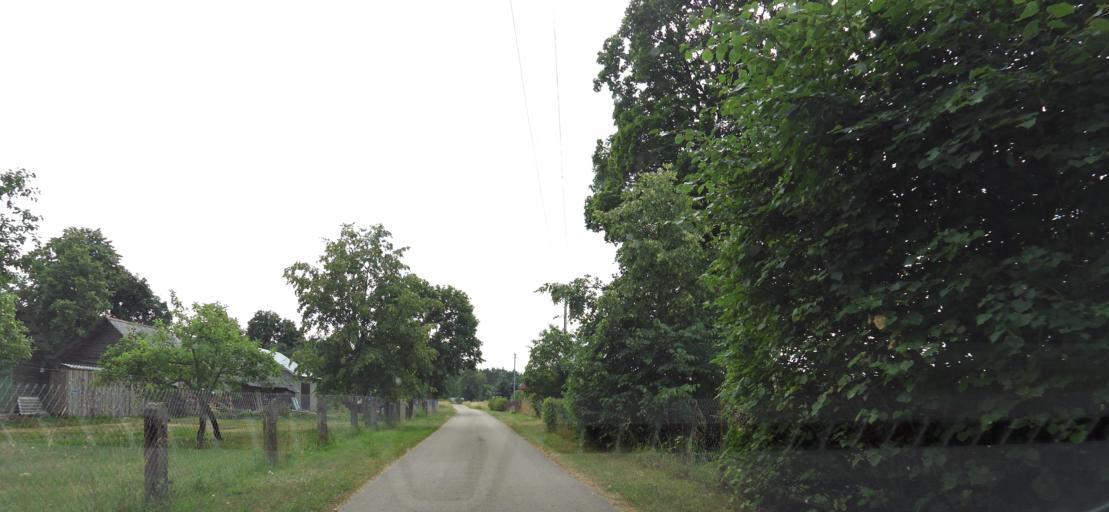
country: LT
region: Vilnius County
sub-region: Trakai
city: Rudiskes
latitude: 54.4004
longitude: 24.9540
